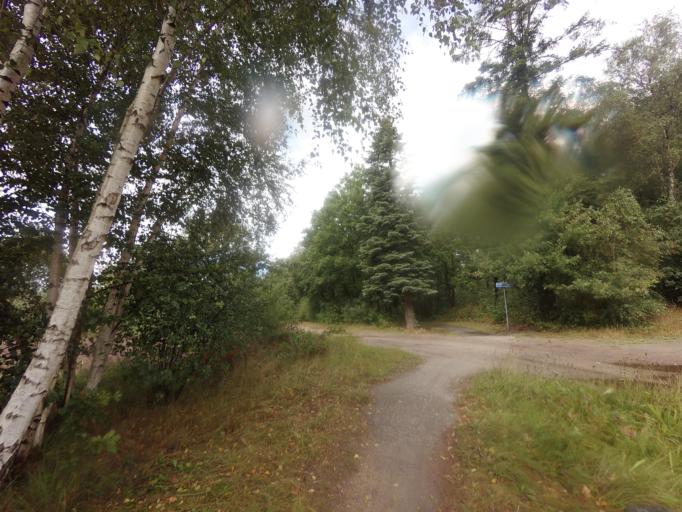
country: NL
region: Overijssel
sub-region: Gemeente Staphorst
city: Staphorst
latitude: 52.6126
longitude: 6.3311
